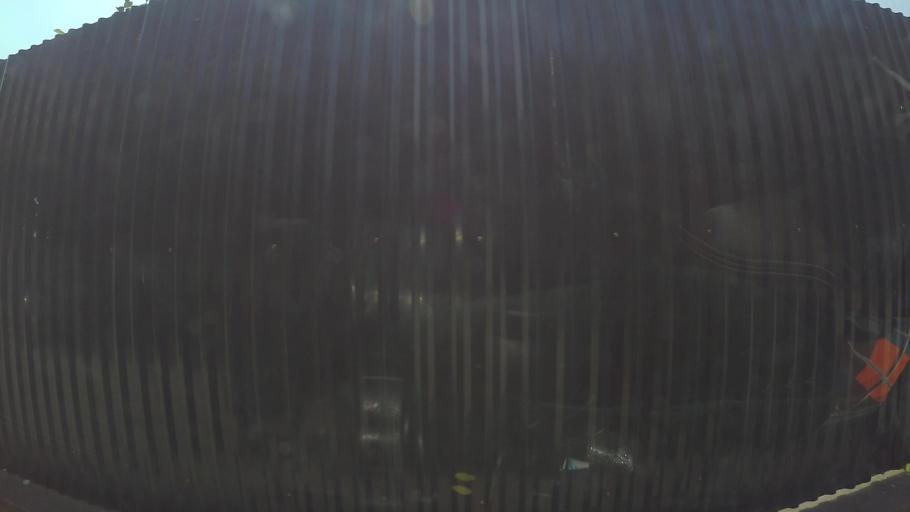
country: VN
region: Ha Noi
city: Trau Quy
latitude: 21.0284
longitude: 105.9085
